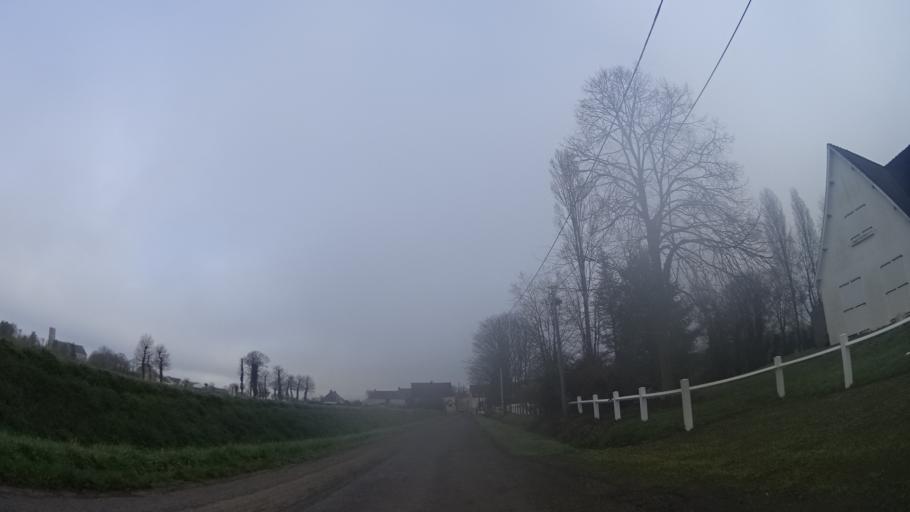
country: FR
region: Brittany
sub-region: Departement d'Ille-et-Vilaine
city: Saint-Domineuc
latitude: 48.3354
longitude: -1.9293
